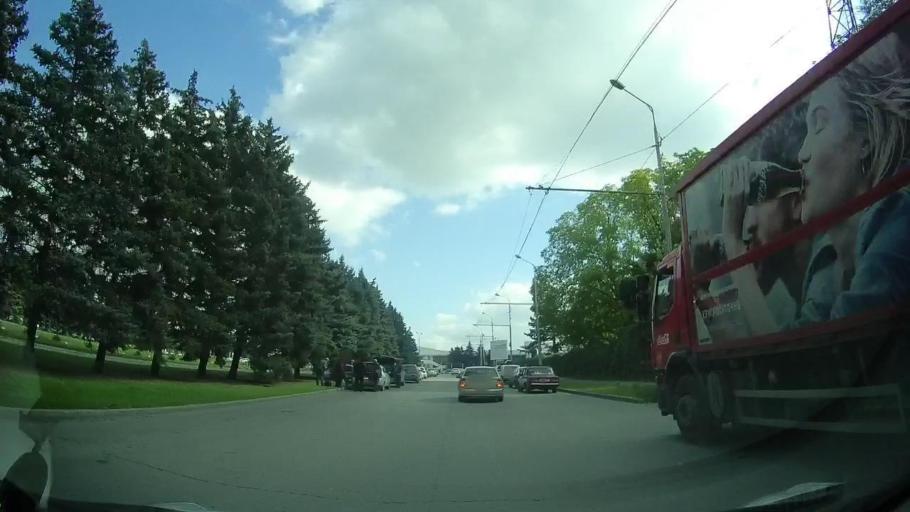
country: RU
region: Rostov
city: Imeni Chkalova
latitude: 47.2562
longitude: 39.8012
